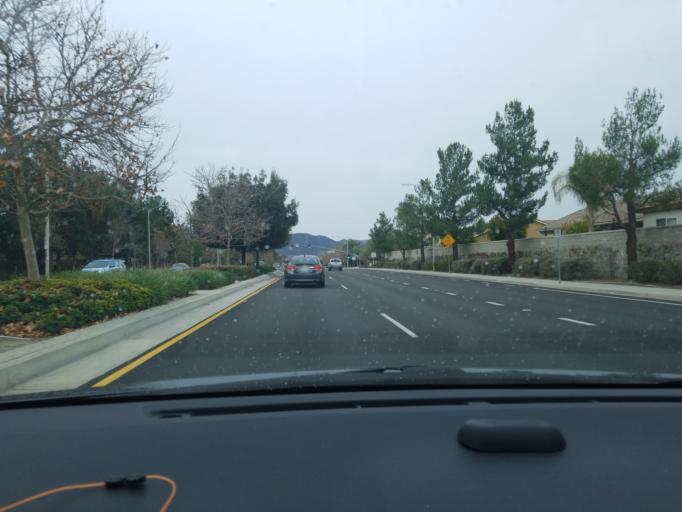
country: US
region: California
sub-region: Riverside County
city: Murrieta Hot Springs
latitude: 33.5421
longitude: -117.1590
